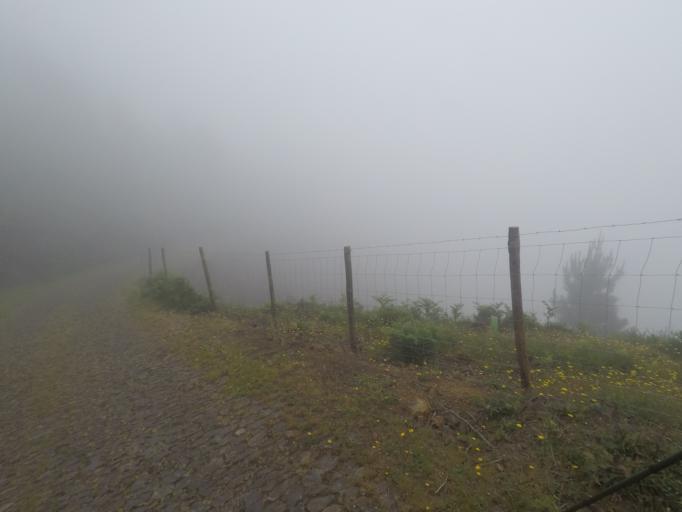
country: PT
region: Madeira
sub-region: Calheta
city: Arco da Calheta
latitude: 32.7321
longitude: -17.0970
